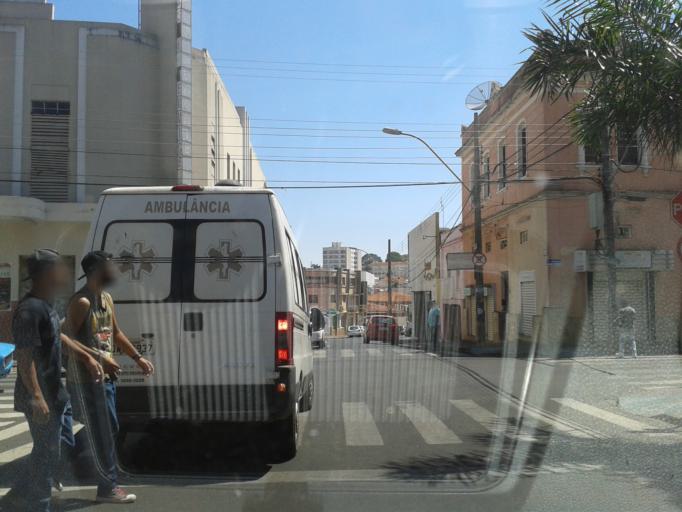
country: BR
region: Minas Gerais
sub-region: Araguari
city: Araguari
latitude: -18.6486
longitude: -48.1903
